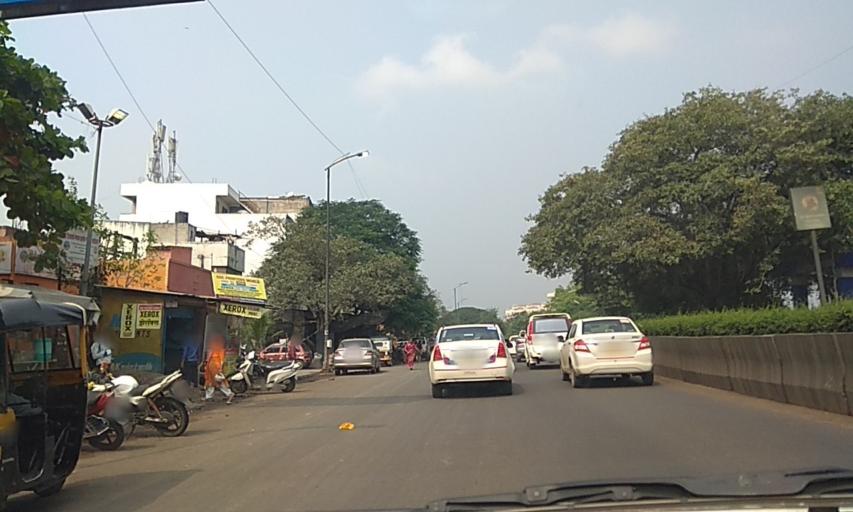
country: IN
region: Maharashtra
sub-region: Pune Division
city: Khadki
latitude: 18.5532
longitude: 73.8851
